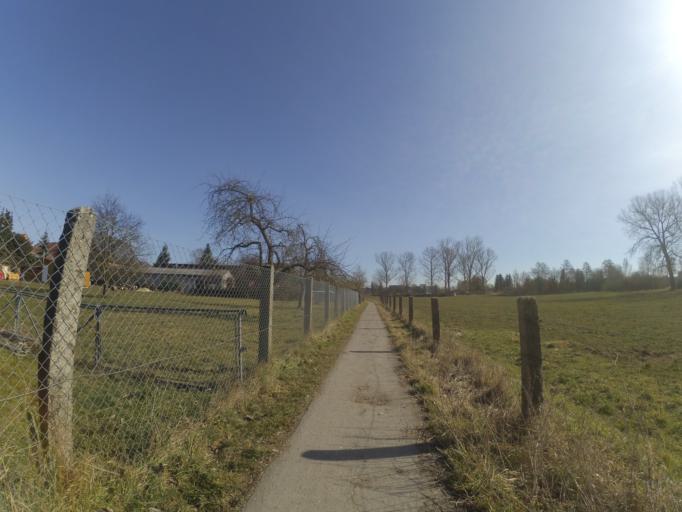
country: DE
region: Baden-Wuerttemberg
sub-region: Tuebingen Region
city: Langenau
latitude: 48.5027
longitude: 10.1324
